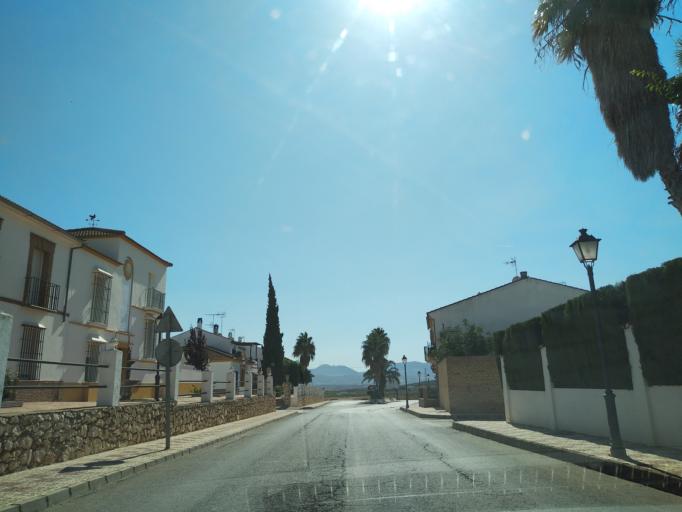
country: ES
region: Andalusia
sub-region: Provincia de Malaga
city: Mollina
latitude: 37.1222
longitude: -4.6548
